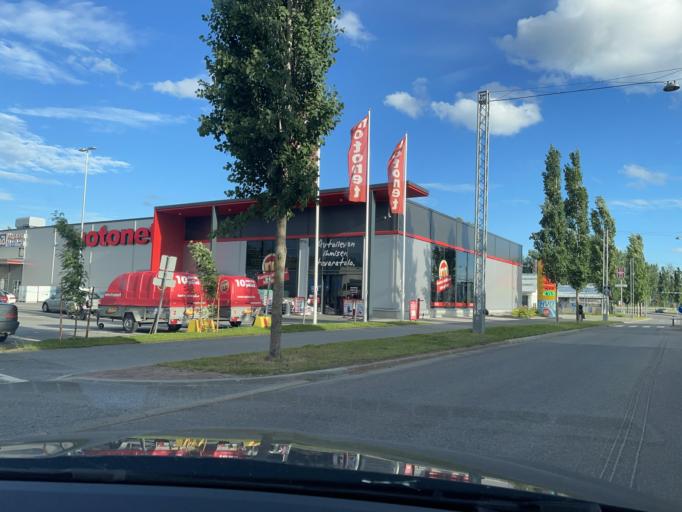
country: FI
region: Central Finland
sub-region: Jyvaeskylae
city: Jyvaeskylae
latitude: 62.2558
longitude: 25.7773
